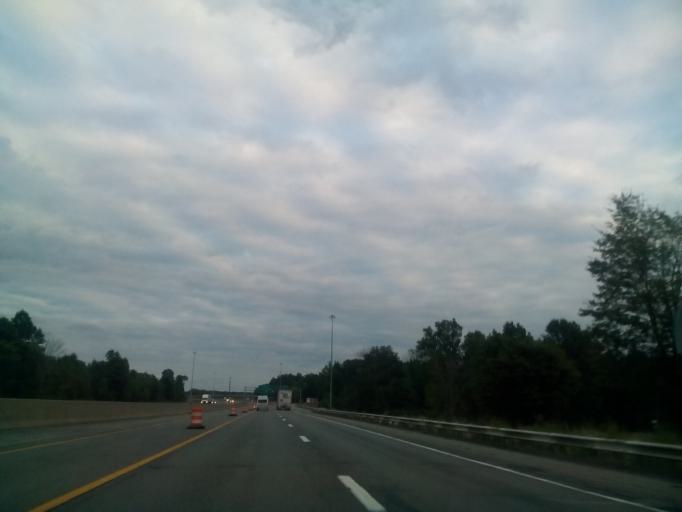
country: US
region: Ohio
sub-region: Trumbull County
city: Lordstown
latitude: 41.1561
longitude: -80.8985
